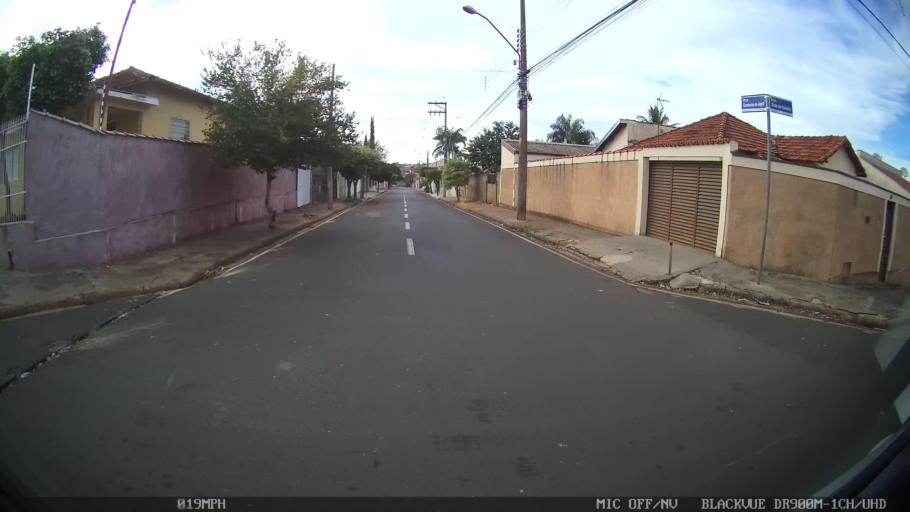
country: BR
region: Sao Paulo
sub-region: Catanduva
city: Catanduva
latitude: -21.1271
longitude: -48.9666
